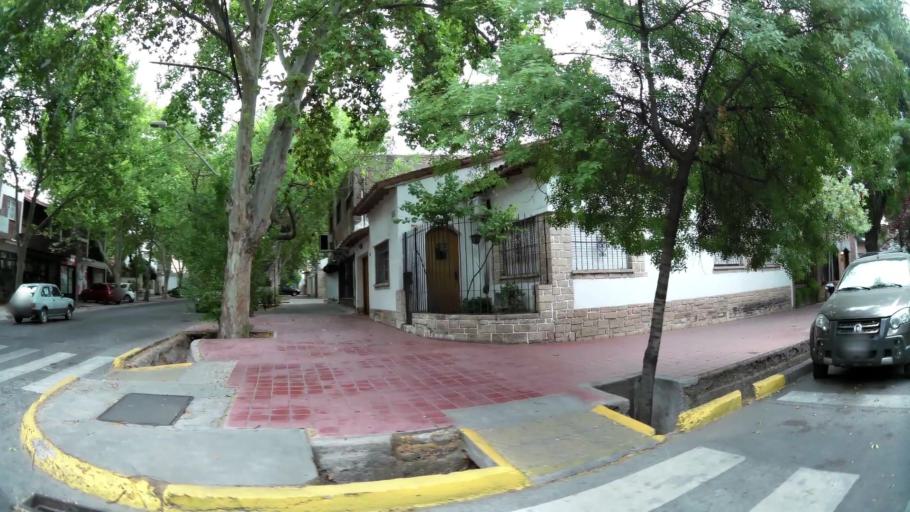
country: AR
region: Mendoza
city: Mendoza
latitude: -32.8897
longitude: -68.8565
